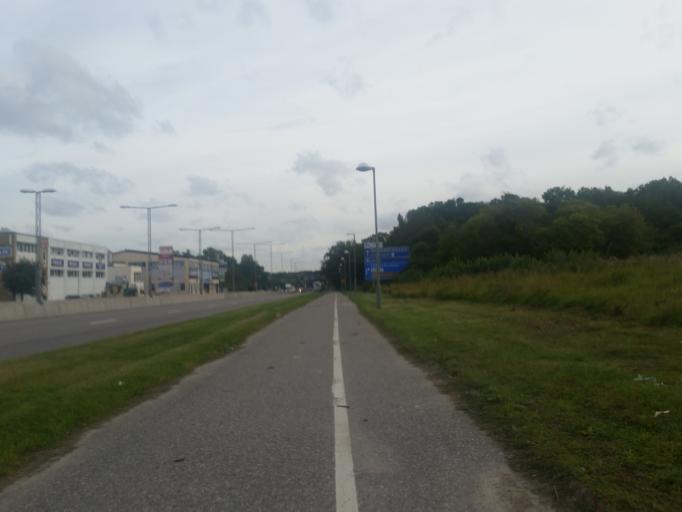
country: SE
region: Stockholm
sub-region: Stockholms Kommun
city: Bromma
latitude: 59.3477
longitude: 17.9573
